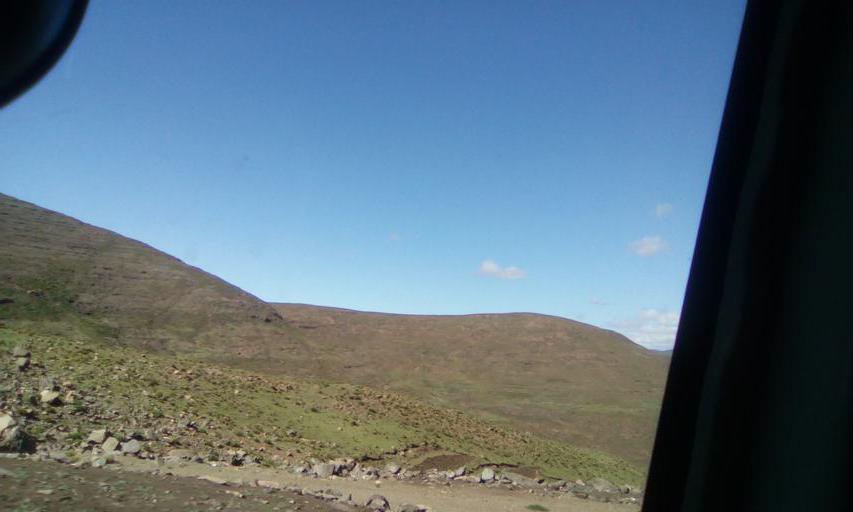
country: LS
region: Maseru
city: Nako
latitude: -29.8890
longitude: 28.1128
